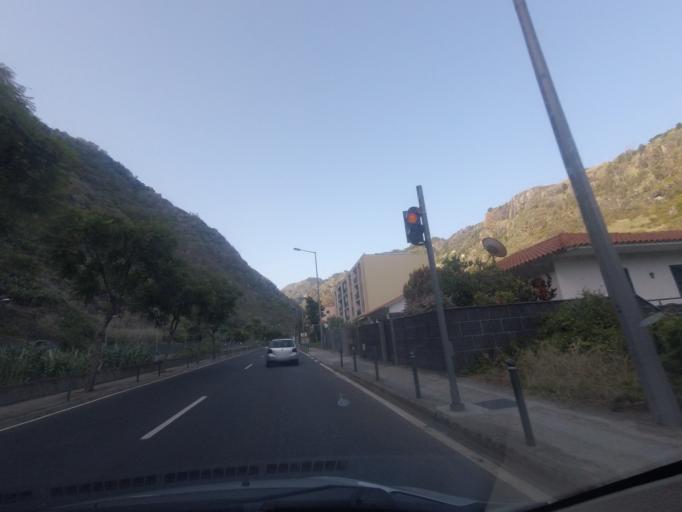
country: PT
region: Madeira
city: Ribeira Brava
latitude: 32.6775
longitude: -17.0619
